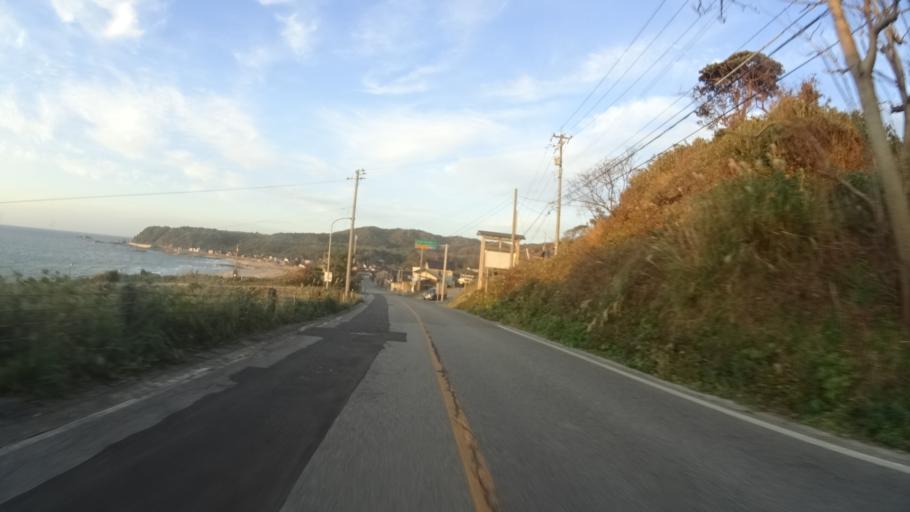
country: JP
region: Ishikawa
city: Nanao
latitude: 37.2263
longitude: 136.7047
